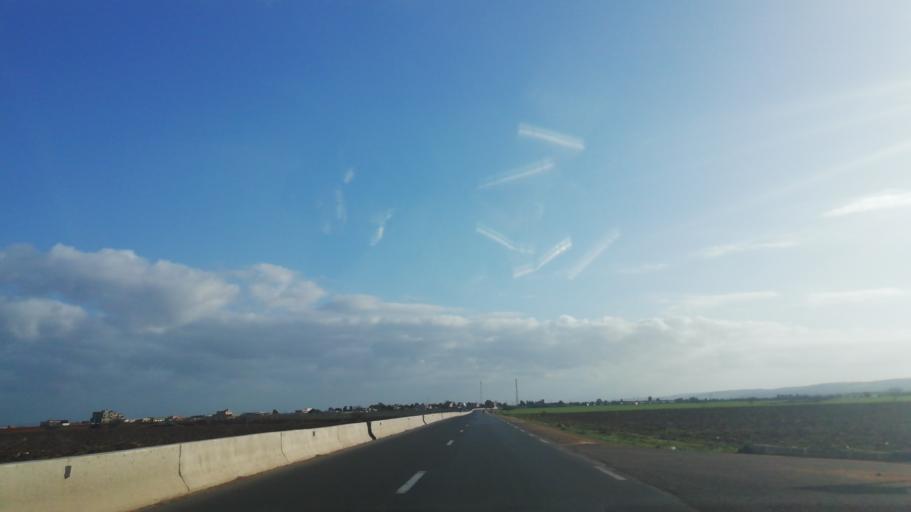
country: DZ
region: Mostaganem
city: Mostaganem
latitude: 36.1091
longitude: 0.3111
